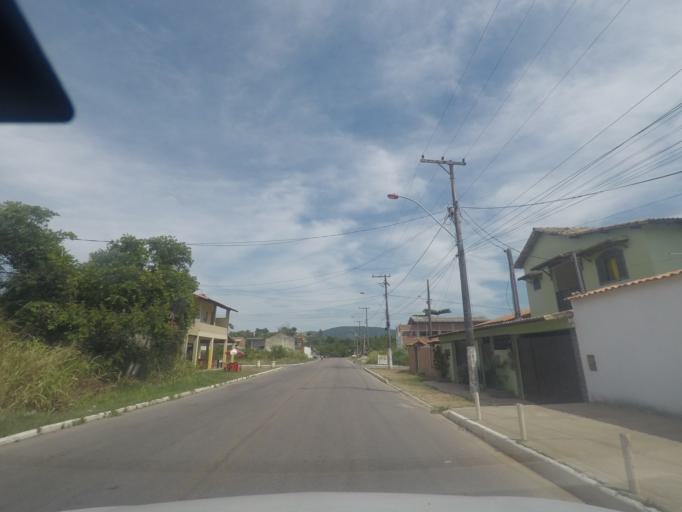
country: BR
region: Rio de Janeiro
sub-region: Marica
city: Marica
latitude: -22.9476
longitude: -42.7521
